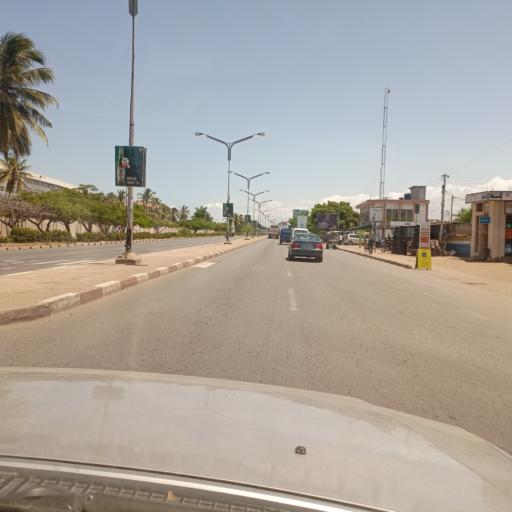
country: TG
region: Maritime
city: Lome
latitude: 6.1382
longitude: 1.2665
